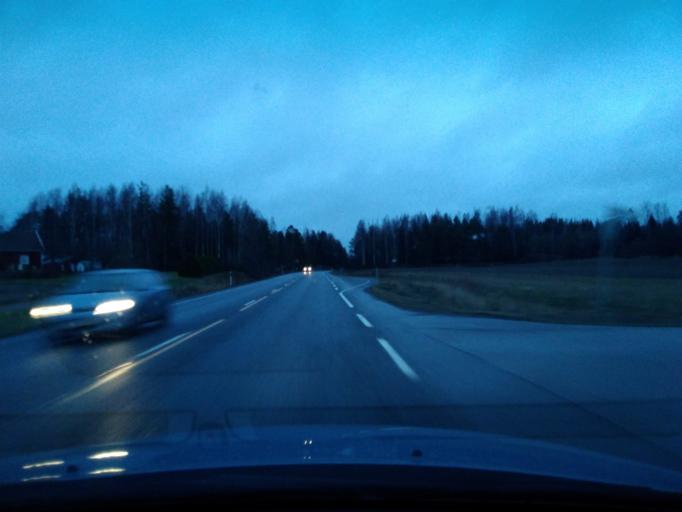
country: FI
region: Uusimaa
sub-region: Porvoo
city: Porvoo
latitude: 60.4164
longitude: 25.5800
